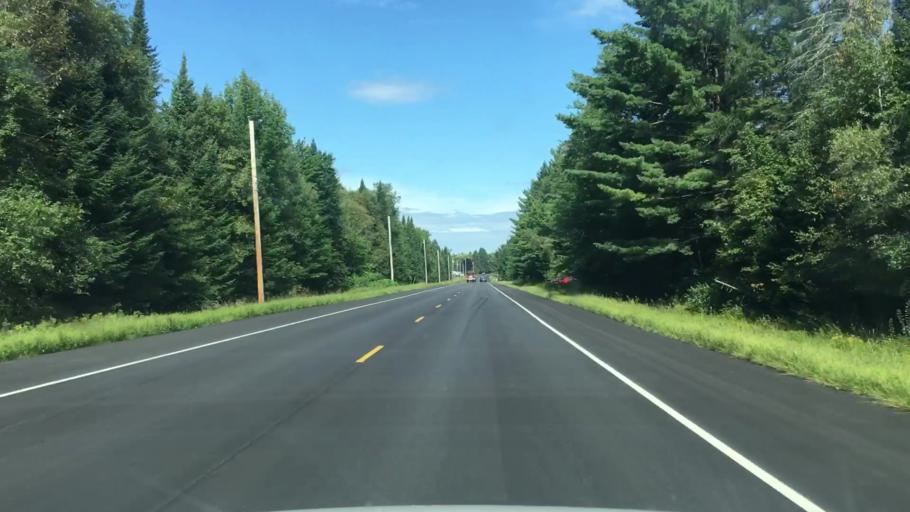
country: US
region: Maine
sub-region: Penobscot County
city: Corinna
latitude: 44.9638
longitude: -69.2708
